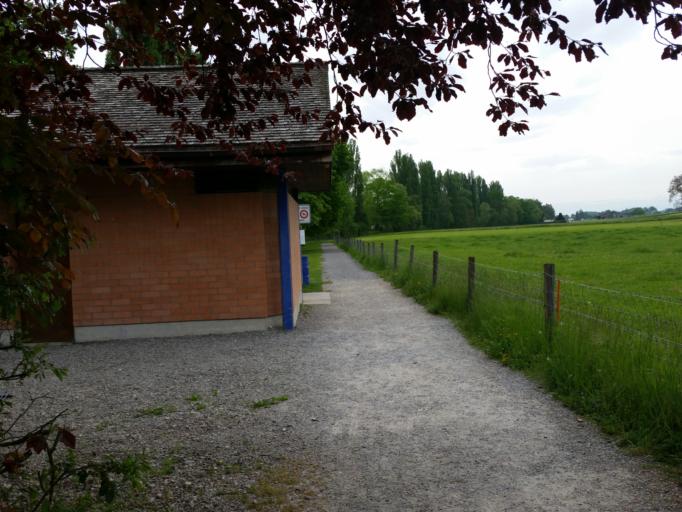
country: CH
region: Thurgau
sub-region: Kreuzlingen District
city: Altnau
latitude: 47.6204
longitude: 9.2739
